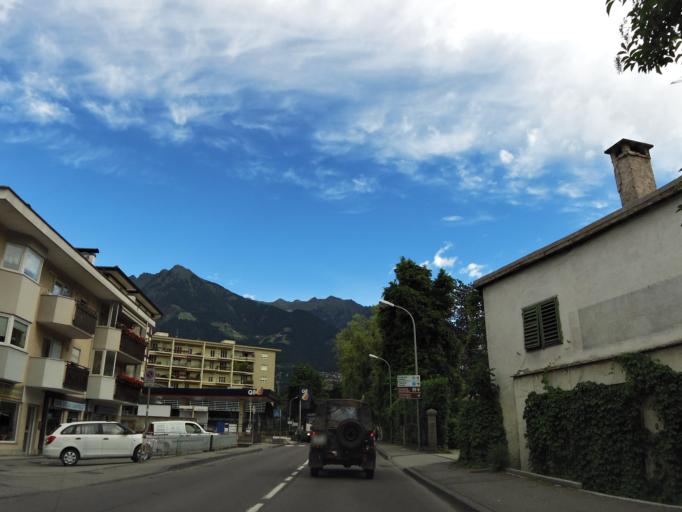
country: IT
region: Trentino-Alto Adige
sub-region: Bolzano
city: Merano
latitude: 46.6648
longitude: 11.1589
